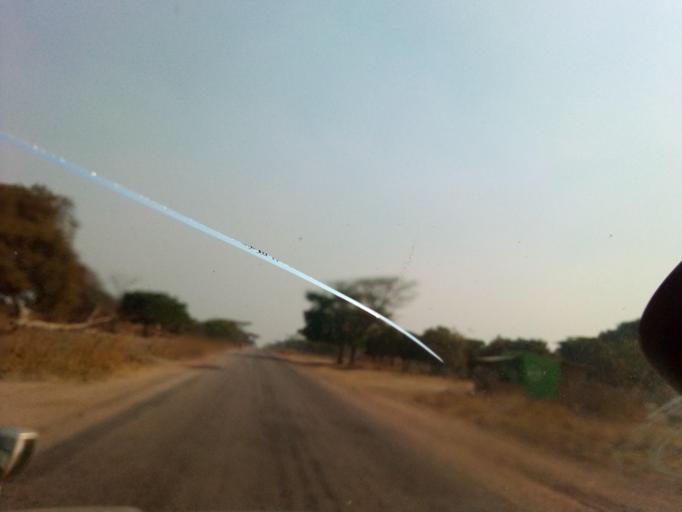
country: ZM
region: Northern
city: Chinsali
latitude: -10.9363
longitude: 32.0411
